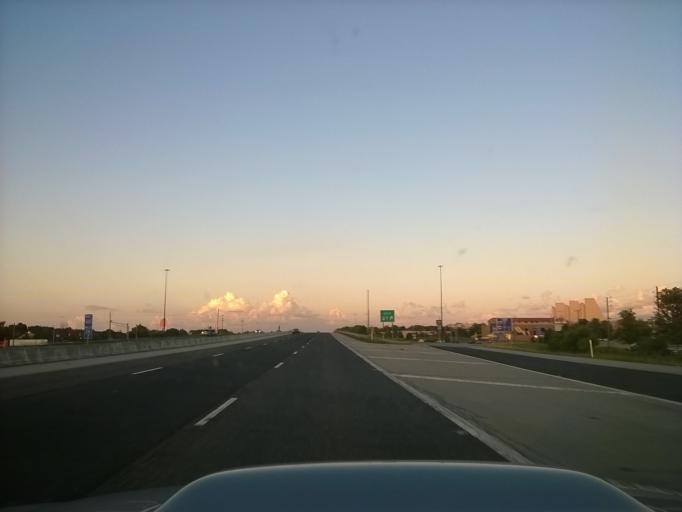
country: US
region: Indiana
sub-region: Boone County
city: Zionsville
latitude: 39.9235
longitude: -86.2321
